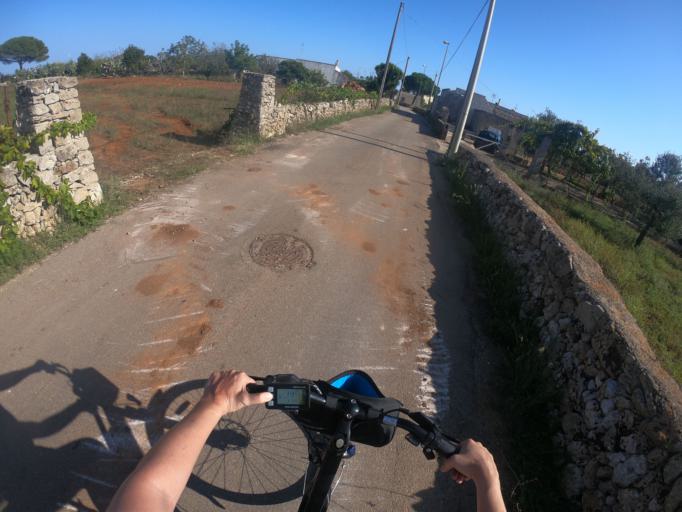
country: IT
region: Apulia
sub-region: Provincia di Lecce
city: Alessano
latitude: 39.8897
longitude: 18.3224
